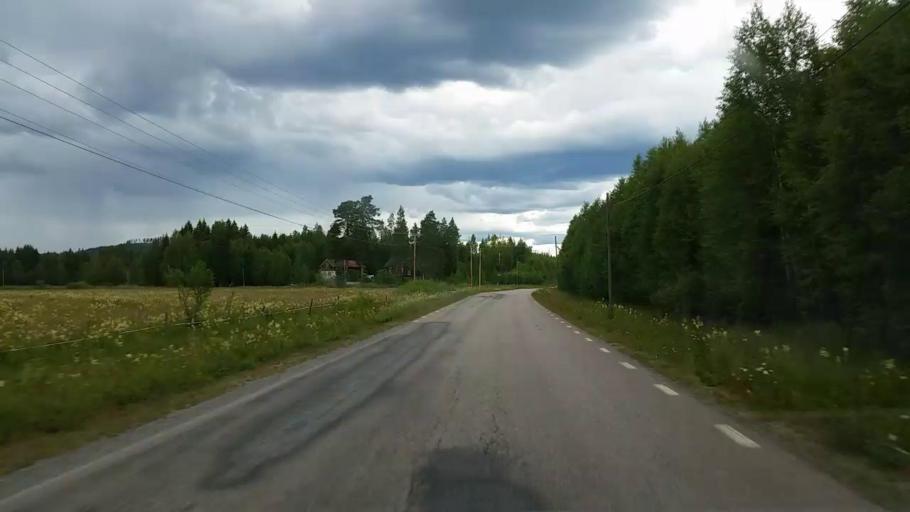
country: SE
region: Gaevleborg
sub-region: Ovanakers Kommun
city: Edsbyn
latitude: 61.4565
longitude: 15.8765
